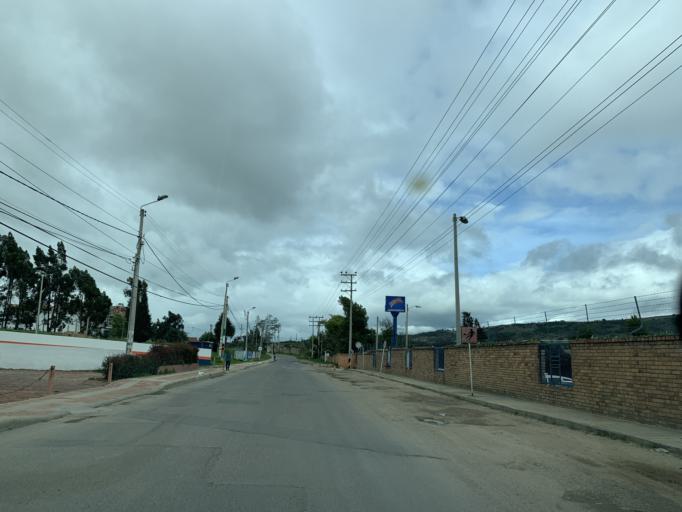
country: CO
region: Boyaca
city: Tunja
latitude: 5.5629
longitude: -73.3449
